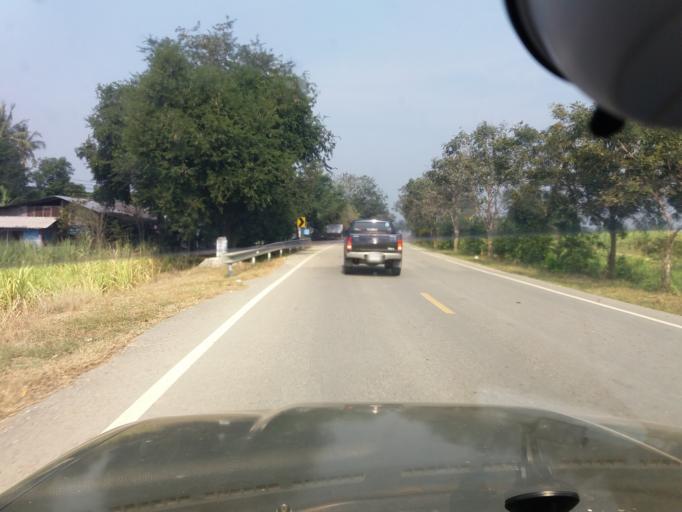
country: TH
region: Sing Buri
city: Bang Racham
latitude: 14.8864
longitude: 100.2727
